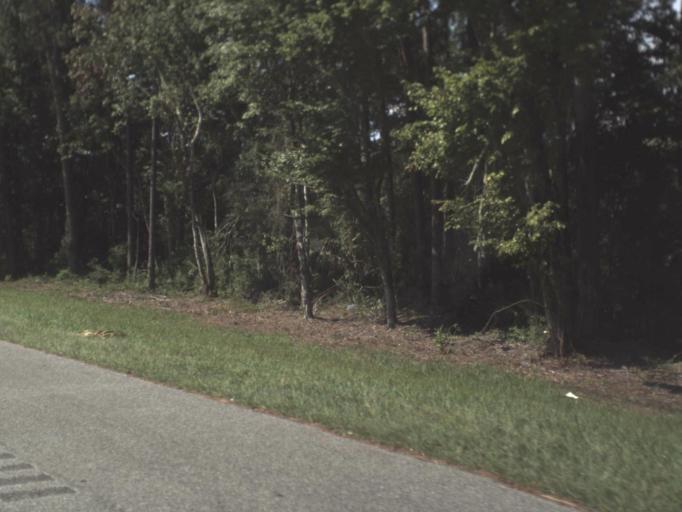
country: US
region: Florida
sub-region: Saint Johns County
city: Fruit Cove
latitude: 30.0309
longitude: -81.4890
